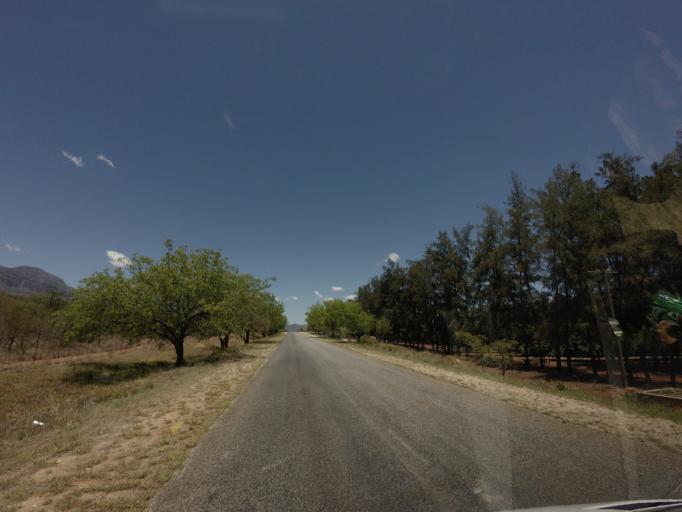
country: ZA
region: Limpopo
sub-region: Mopani District Municipality
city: Hoedspruit
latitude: -24.3740
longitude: 30.7071
